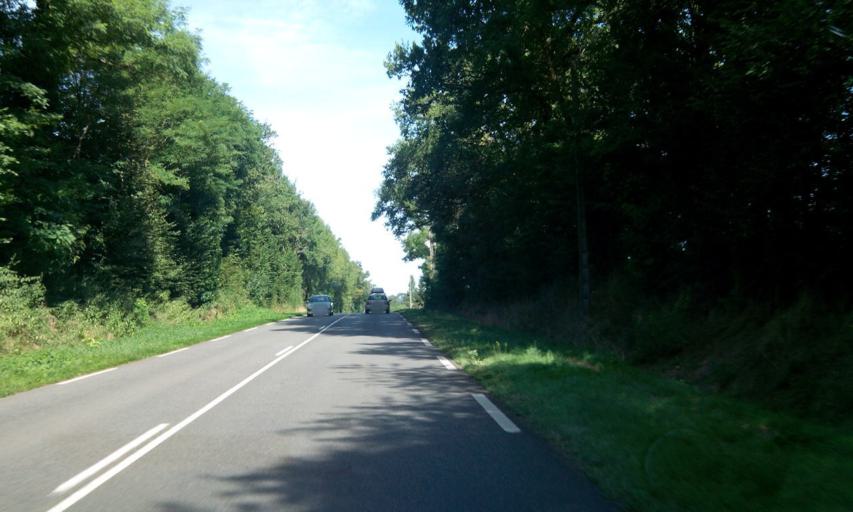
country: FR
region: Poitou-Charentes
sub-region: Departement de la Charente
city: Confolens
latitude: 45.9693
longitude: 0.6935
